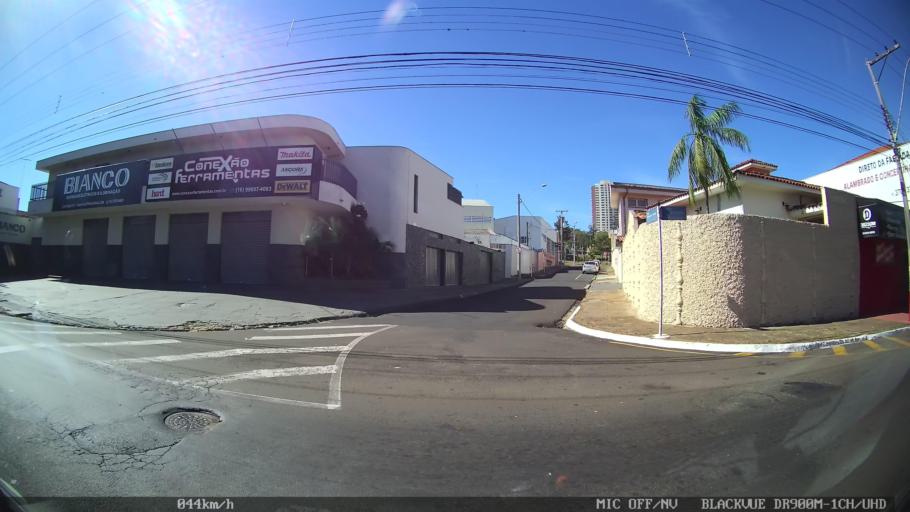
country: BR
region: Sao Paulo
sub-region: Franca
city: Franca
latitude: -20.5233
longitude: -47.4006
